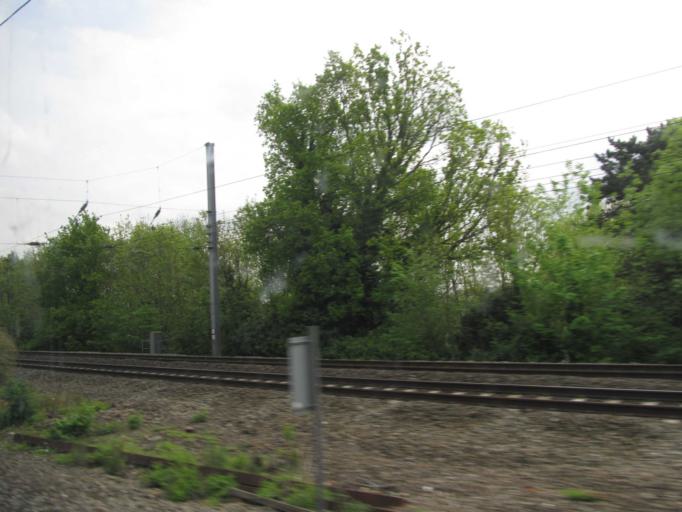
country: GB
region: England
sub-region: Greater London
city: Greenford
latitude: 51.5115
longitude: -0.3405
